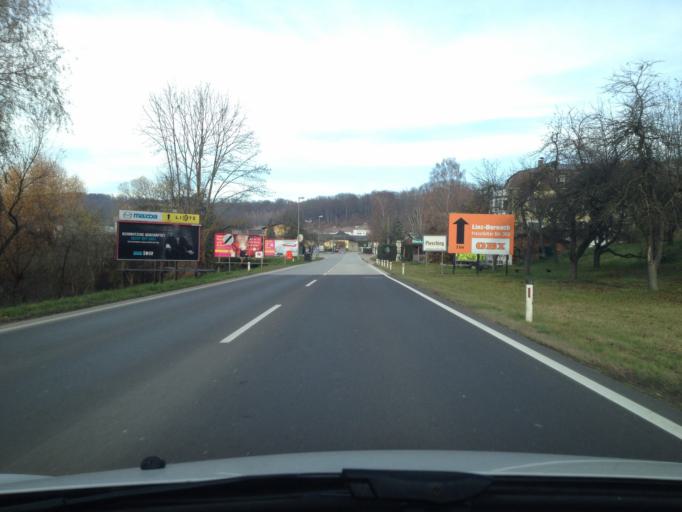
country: AT
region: Upper Austria
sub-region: Politischer Bezirk Urfahr-Umgebung
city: Steyregg
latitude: 48.3178
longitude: 14.3385
